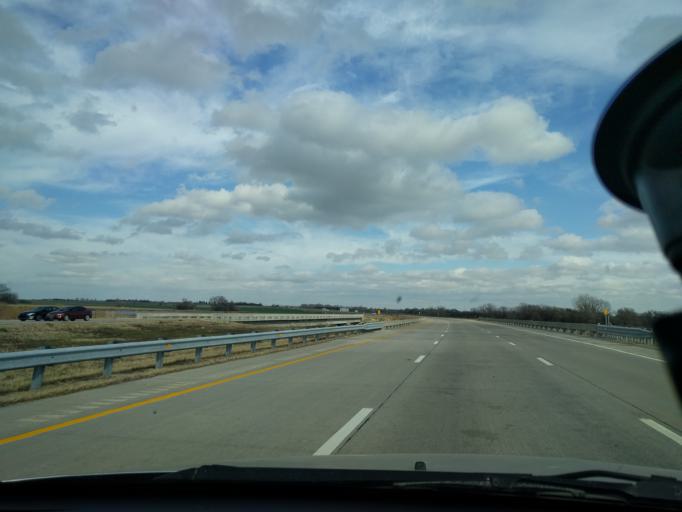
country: US
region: Kansas
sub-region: Reno County
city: Buhler
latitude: 38.1548
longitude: -97.8439
